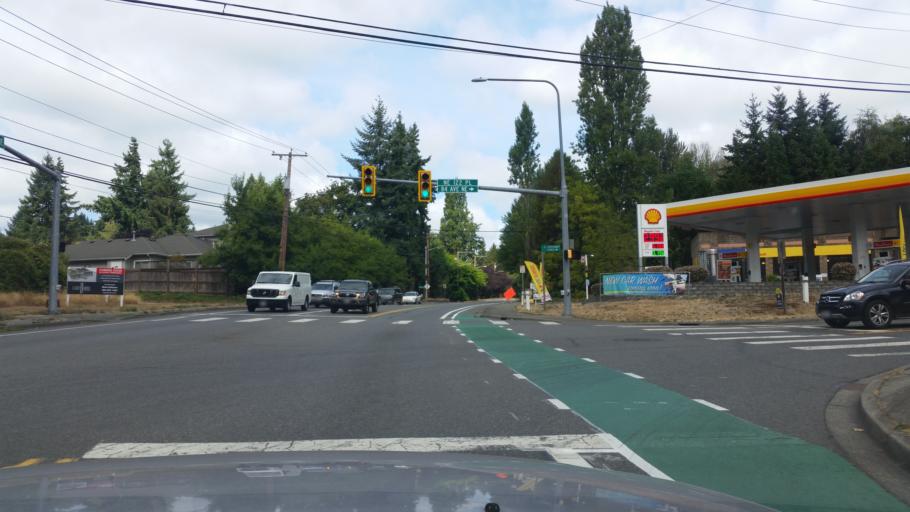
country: US
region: Washington
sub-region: King County
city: Inglewood-Finn Hill
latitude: 47.7092
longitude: -122.2379
